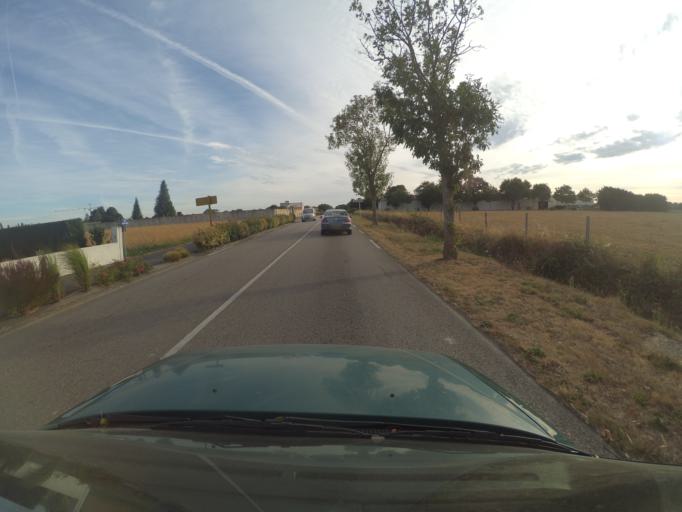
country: FR
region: Pays de la Loire
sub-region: Departement de la Vendee
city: Bouffere
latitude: 46.9575
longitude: -1.3436
